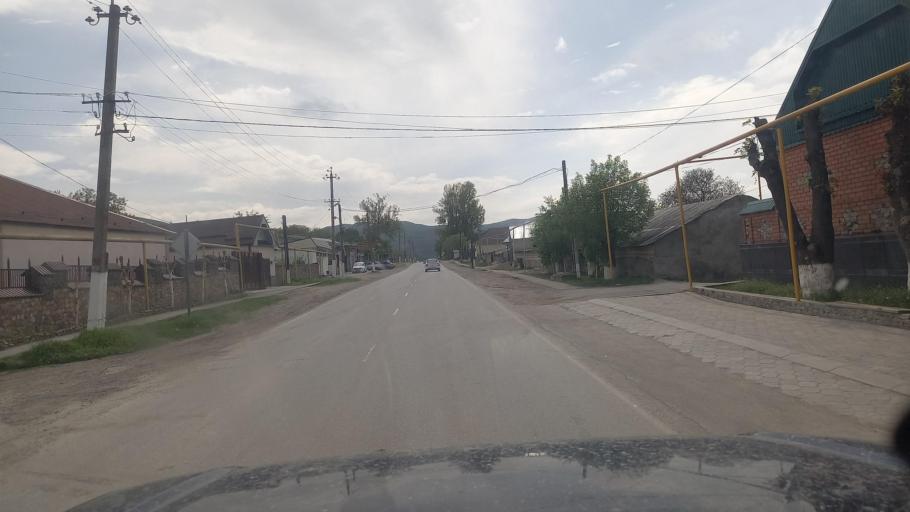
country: RU
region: Kabardino-Balkariya
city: Sarmakovo
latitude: 43.7374
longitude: 43.1813
